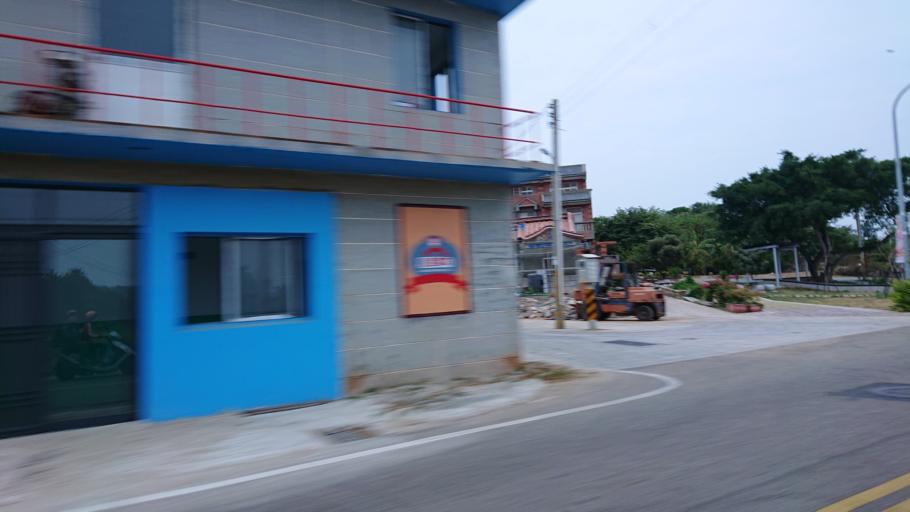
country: TW
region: Fukien
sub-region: Kinmen
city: Jincheng
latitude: 24.4271
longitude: 118.2491
